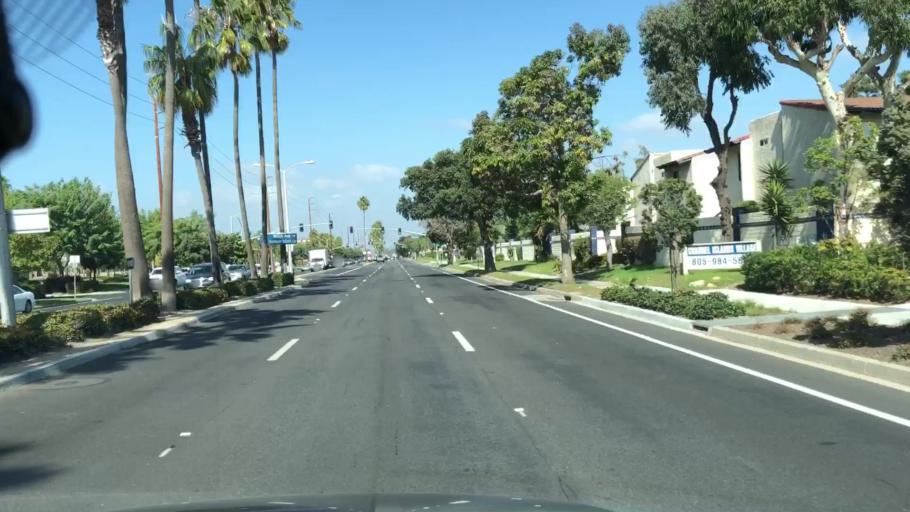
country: US
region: California
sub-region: Ventura County
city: Oxnard Shores
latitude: 34.1826
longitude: -119.2212
